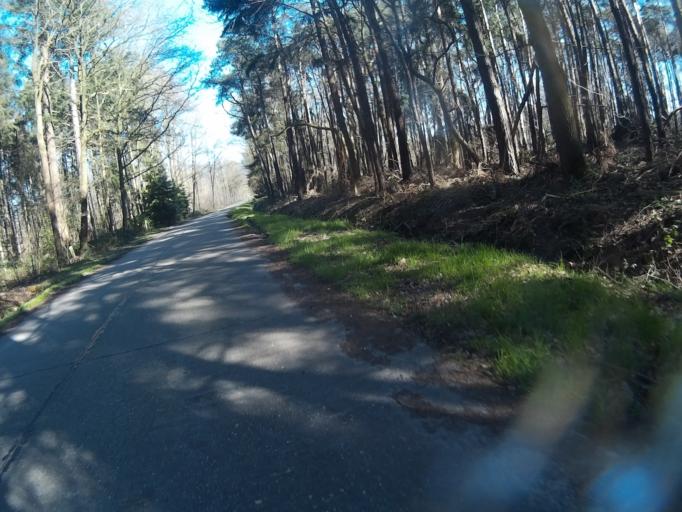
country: BE
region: Flanders
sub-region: Provincie Oost-Vlaanderen
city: Knesselare
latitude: 51.1401
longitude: 3.4528
